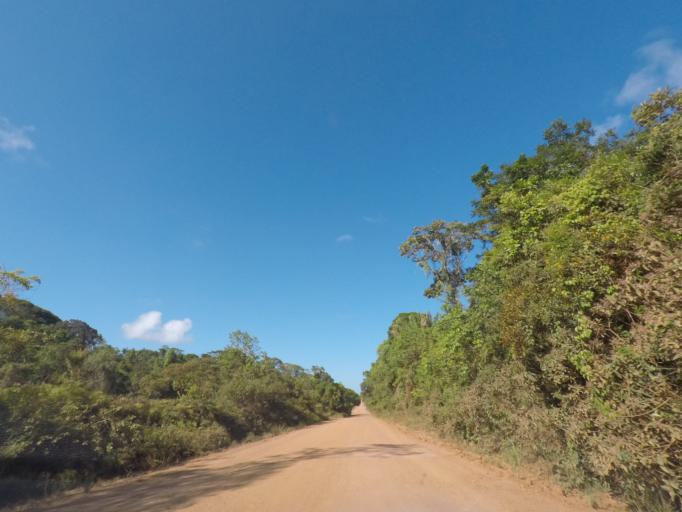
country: BR
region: Bahia
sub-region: Marau
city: Marau
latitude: -14.1202
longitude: -38.9888
